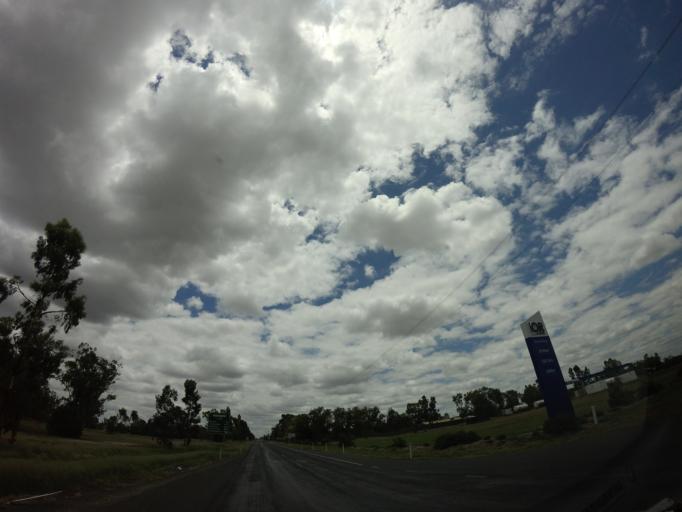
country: AU
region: Queensland
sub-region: Goondiwindi
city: Goondiwindi
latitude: -28.5219
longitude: 150.2877
